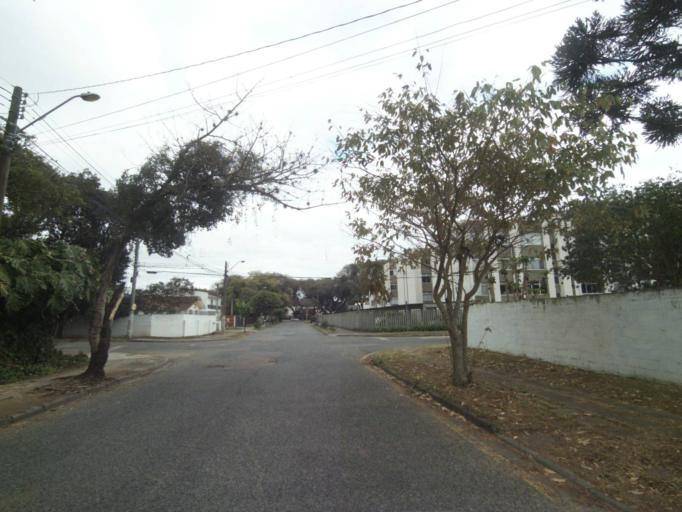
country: BR
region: Parana
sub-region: Curitiba
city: Curitiba
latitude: -25.4568
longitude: -49.3004
